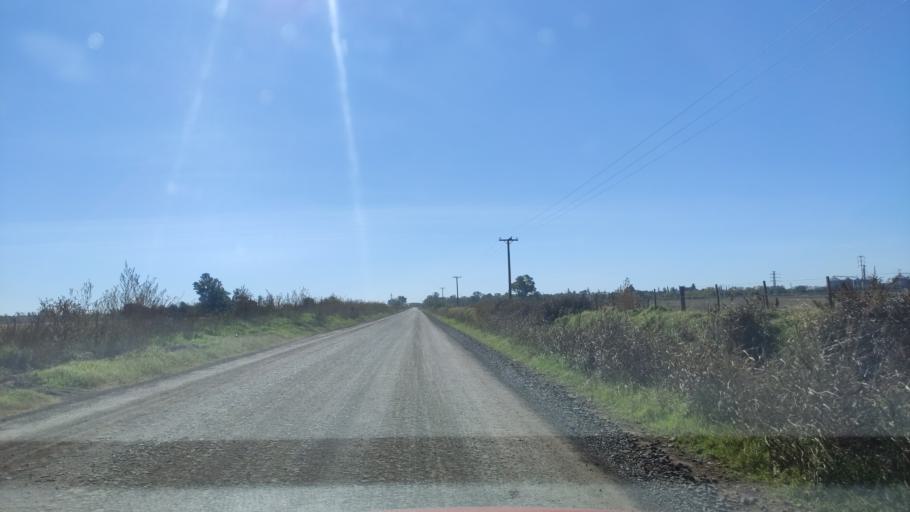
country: AR
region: Cordoba
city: Leones
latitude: -32.6706
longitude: -62.3127
